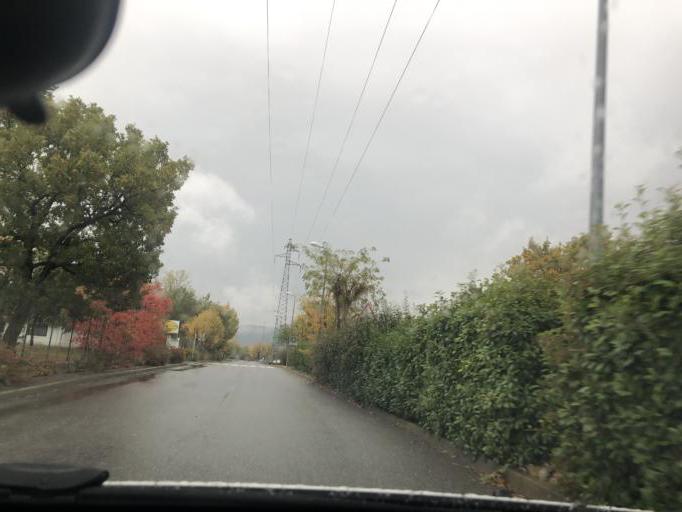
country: FR
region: Provence-Alpes-Cote d'Azur
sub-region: Departement des Alpes-de-Haute-Provence
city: Sisteron
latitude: 44.2299
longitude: 5.9135
